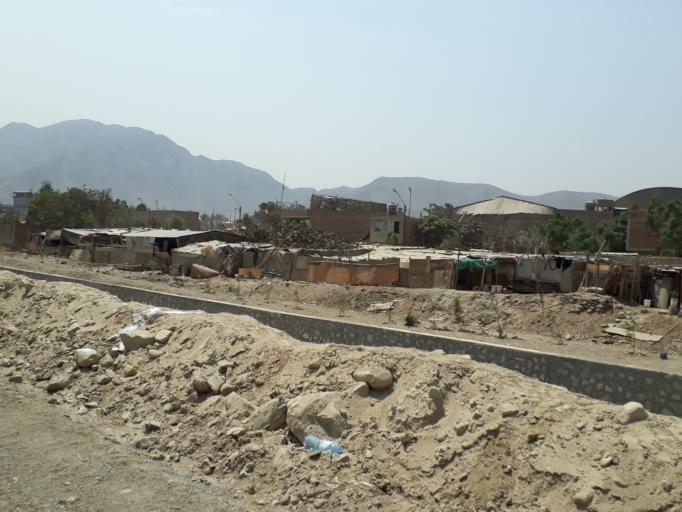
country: PE
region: Lima
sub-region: Lima
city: Santa Maria
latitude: -11.9952
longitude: -76.9105
